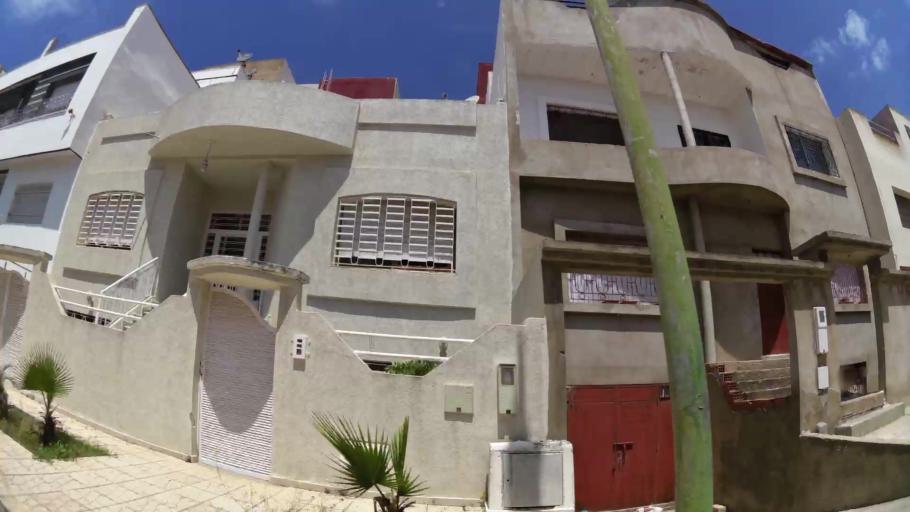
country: MA
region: Gharb-Chrarda-Beni Hssen
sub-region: Kenitra Province
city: Kenitra
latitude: 34.2679
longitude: -6.6108
